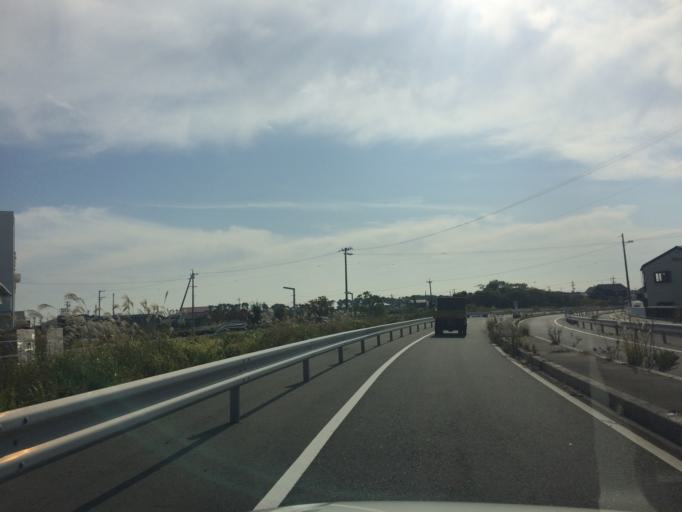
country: JP
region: Shizuoka
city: Fujieda
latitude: 34.7672
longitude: 138.2764
